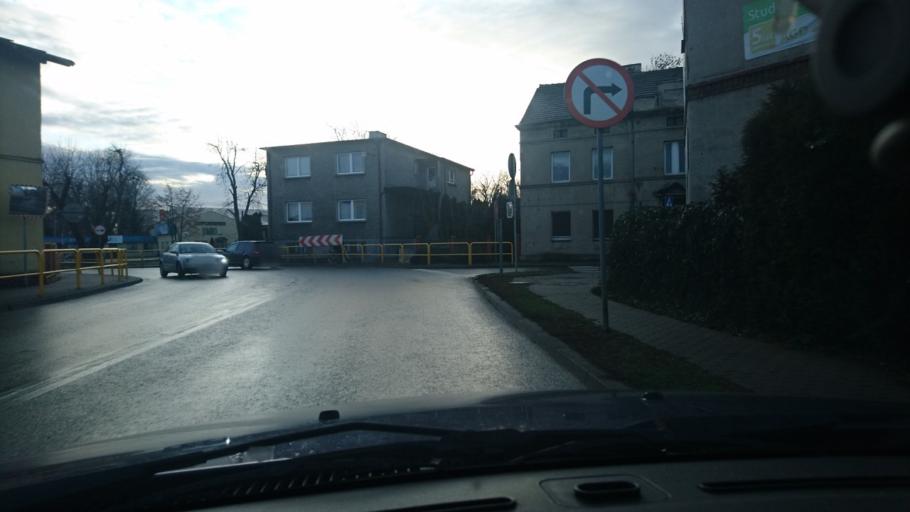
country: PL
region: Greater Poland Voivodeship
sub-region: Powiat kepinski
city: Kepno
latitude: 51.2760
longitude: 17.9899
